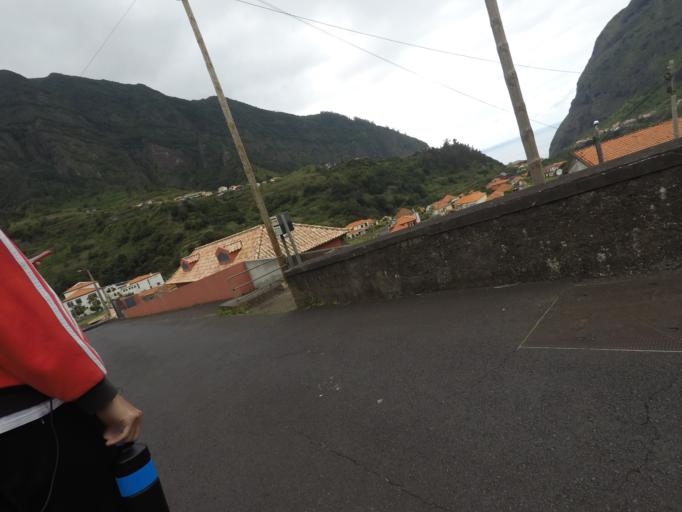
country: PT
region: Madeira
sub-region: Sao Vicente
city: Sao Vicente
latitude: 32.7933
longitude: -17.0410
